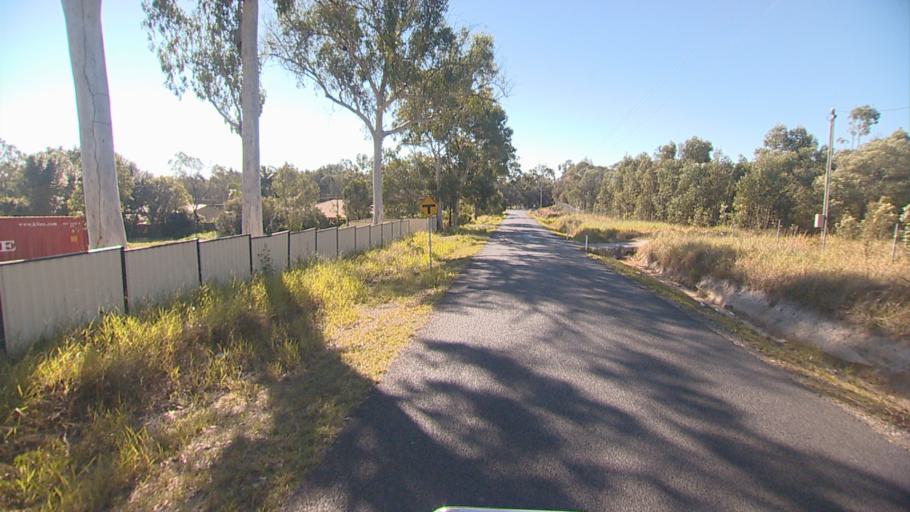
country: AU
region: Queensland
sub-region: Logan
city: Logan Reserve
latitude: -27.7215
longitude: 153.0739
